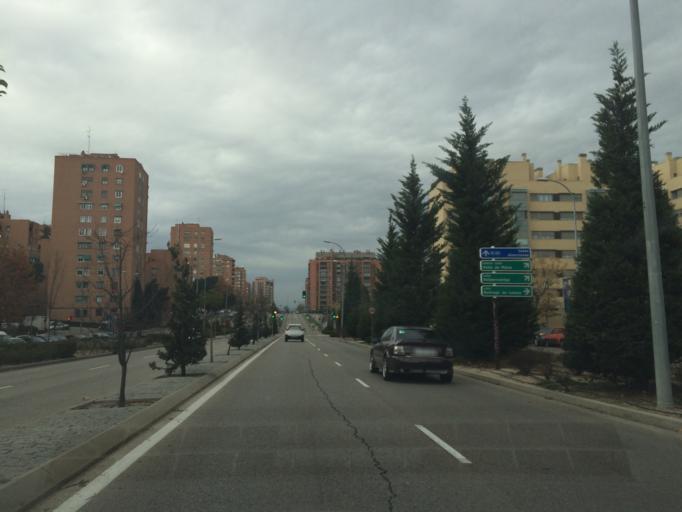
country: ES
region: Madrid
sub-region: Provincia de Madrid
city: Tetuan de las Victorias
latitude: 40.4702
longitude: -3.7162
